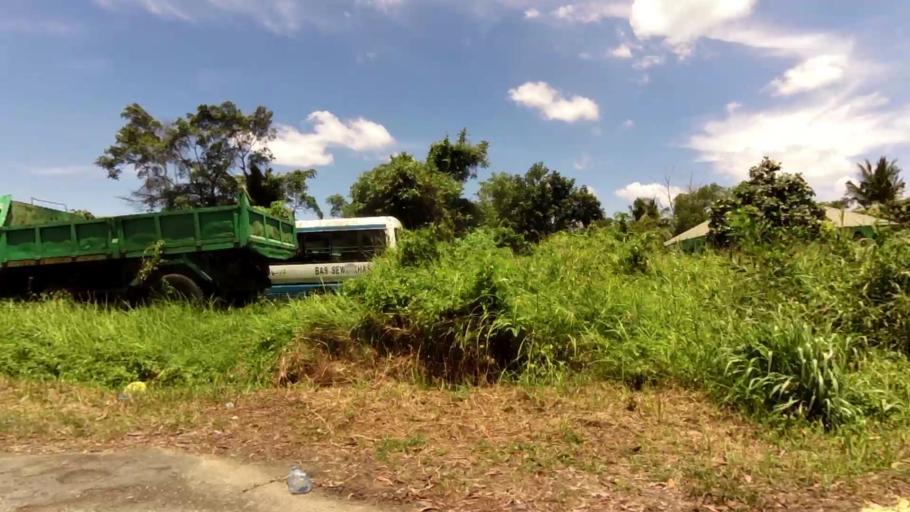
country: BN
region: Brunei and Muara
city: Bandar Seri Begawan
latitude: 4.9435
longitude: 114.9582
